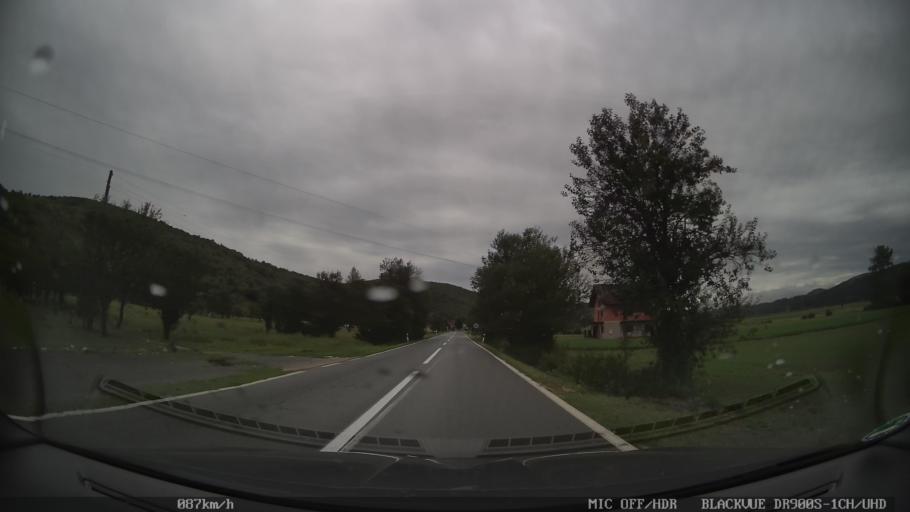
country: HR
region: Licko-Senjska
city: Brinje
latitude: 44.9195
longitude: 15.1479
